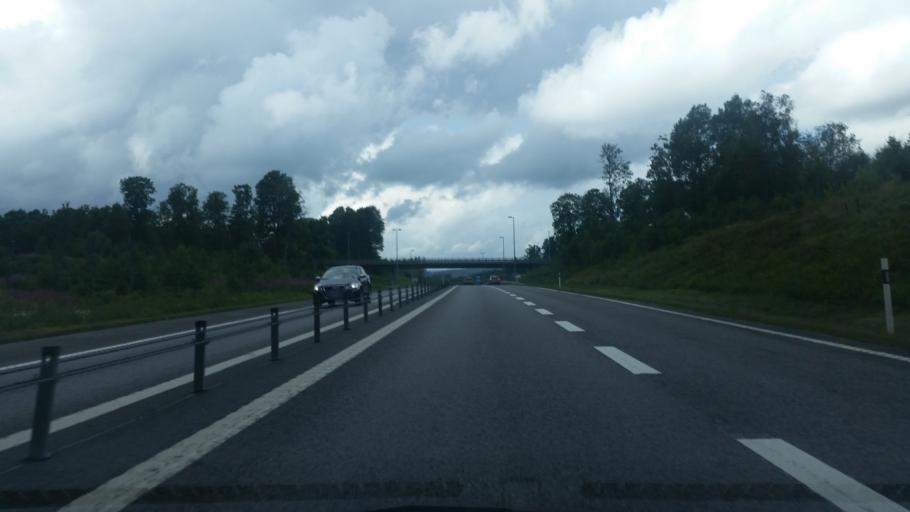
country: SE
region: Vaestra Goetaland
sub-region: Boras Kommun
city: Ganghester
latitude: 57.6477
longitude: 13.0644
